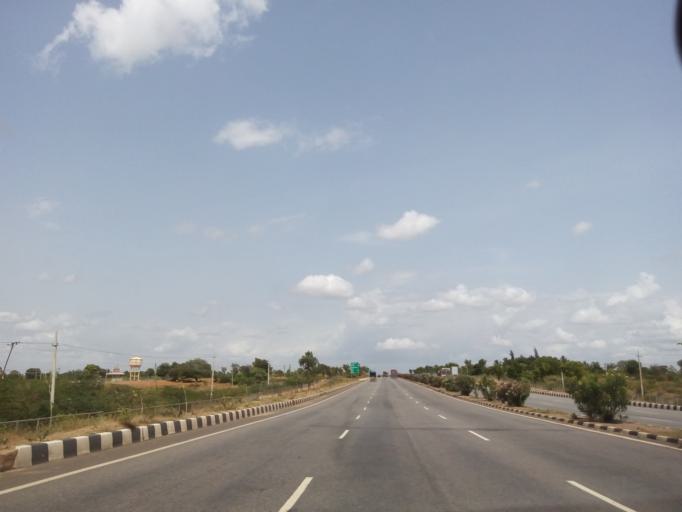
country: IN
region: Karnataka
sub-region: Tumkur
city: Sira
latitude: 13.7232
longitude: 76.9042
